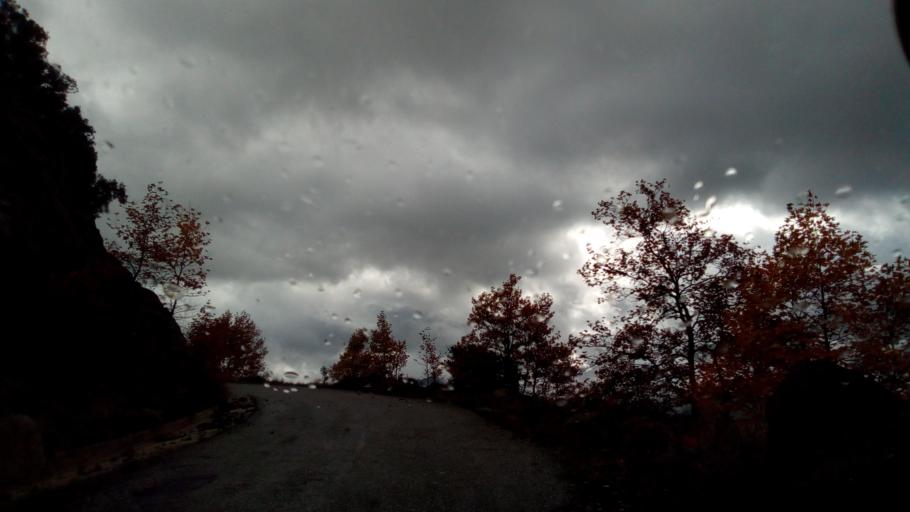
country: GR
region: West Greece
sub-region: Nomos Aitolias kai Akarnanias
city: Thermo
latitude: 38.6835
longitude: 21.8600
